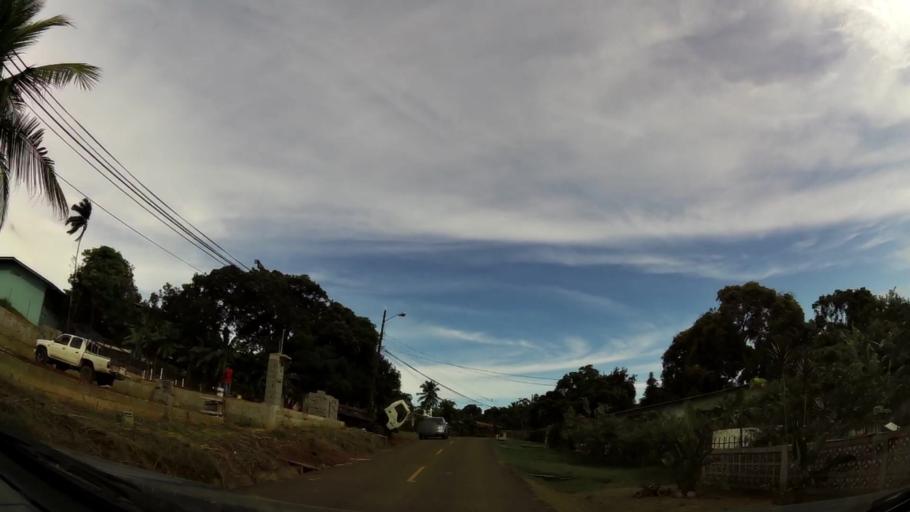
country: PA
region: Panama
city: El Coco
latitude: 8.8663
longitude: -79.8073
